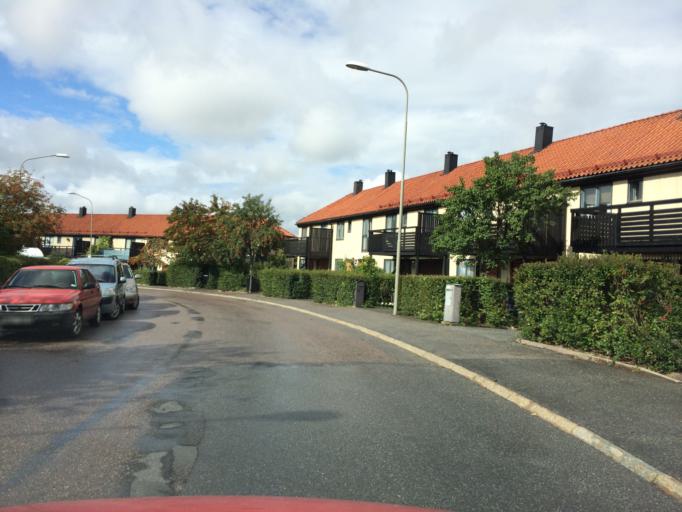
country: SE
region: Stockholm
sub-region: Stockholms Kommun
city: Bromma
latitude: 59.3065
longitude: 17.9754
